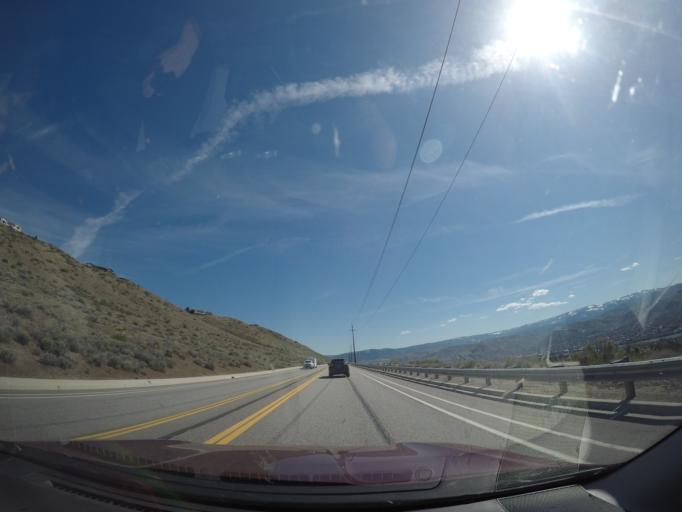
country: US
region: Washington
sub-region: Douglas County
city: East Wenatchee Bench
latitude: 47.4508
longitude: -120.2886
